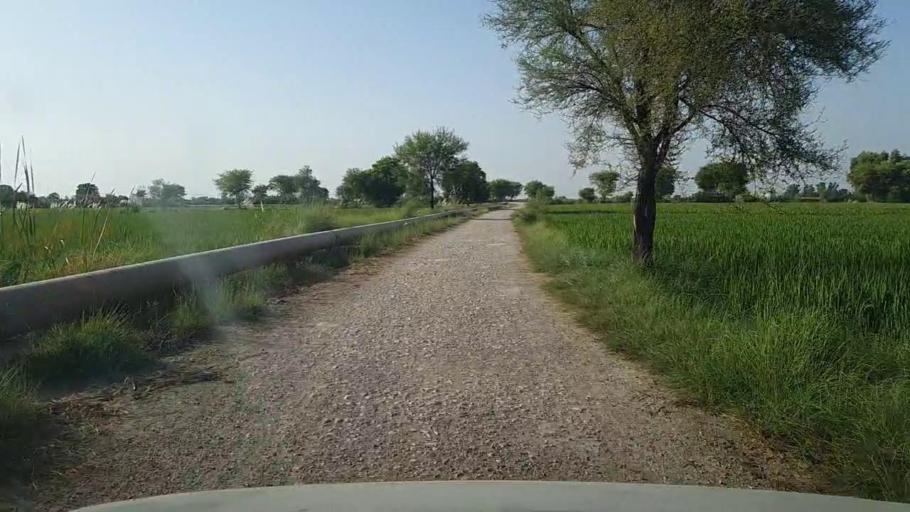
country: PK
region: Sindh
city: Kandhkot
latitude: 28.2874
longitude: 69.3328
